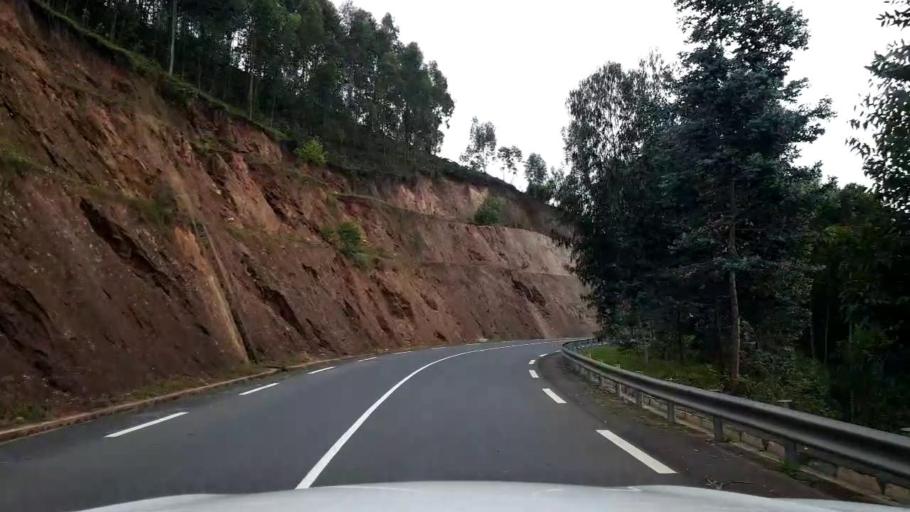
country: RW
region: Western Province
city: Kibuye
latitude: -1.9046
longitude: 29.3565
